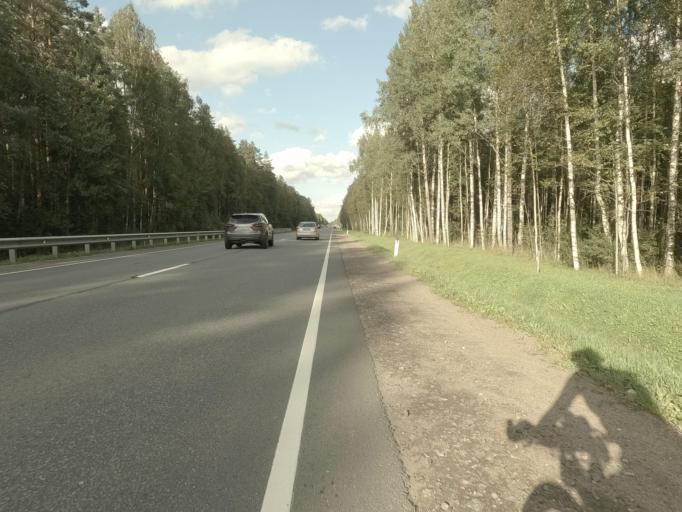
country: RU
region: Leningrad
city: Mga
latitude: 59.7034
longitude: 31.0059
